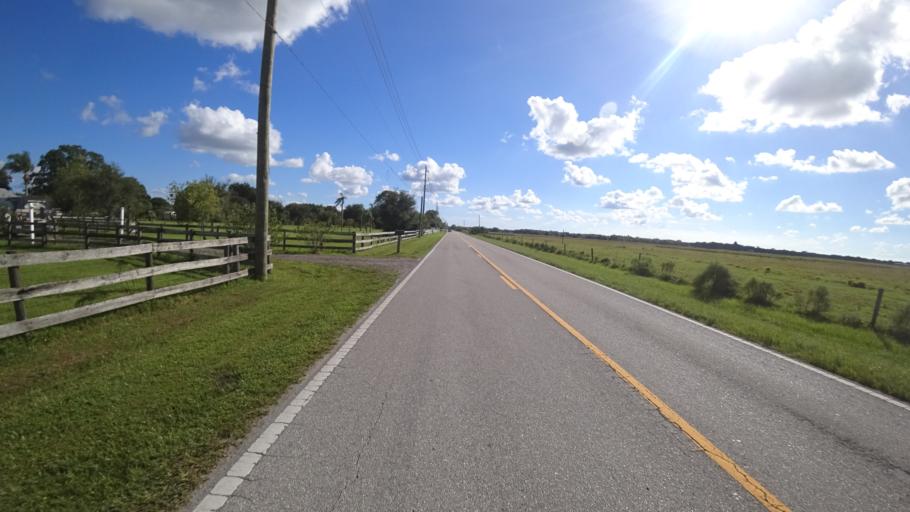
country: US
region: Florida
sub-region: Sarasota County
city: Lake Sarasota
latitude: 27.3410
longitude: -82.2693
